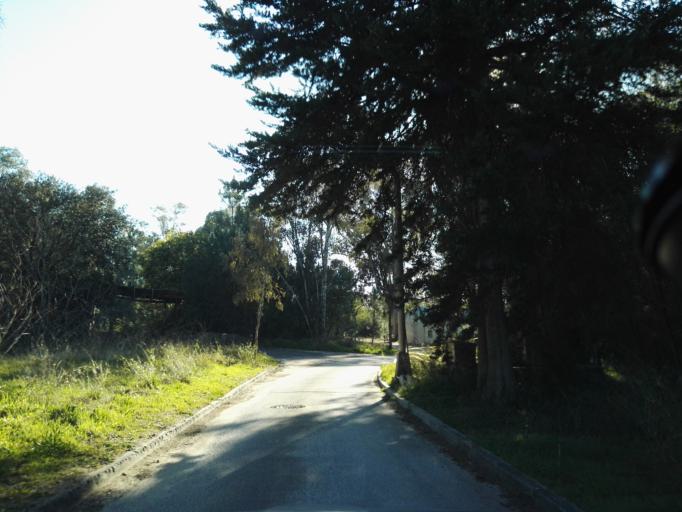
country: PT
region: Setubal
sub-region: Seixal
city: Corroios
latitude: 38.6193
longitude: -9.1464
